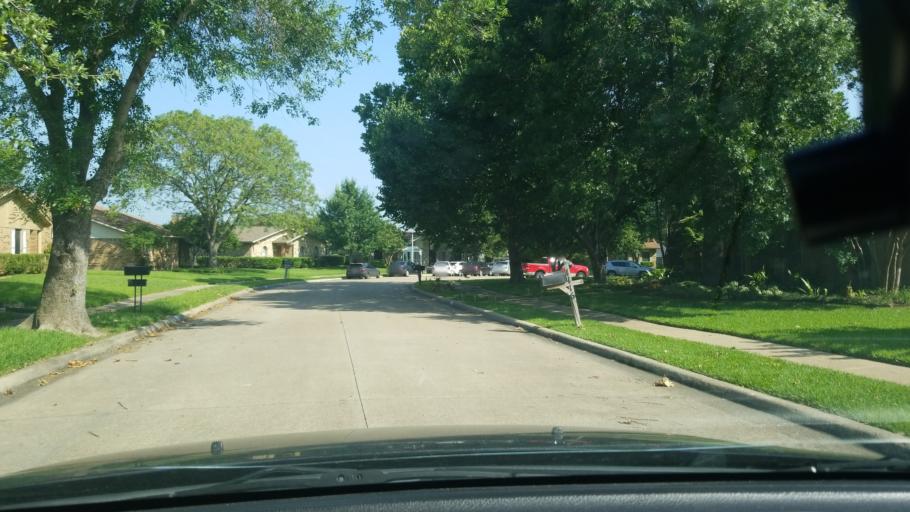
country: US
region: Texas
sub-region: Dallas County
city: Mesquite
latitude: 32.8216
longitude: -96.6142
